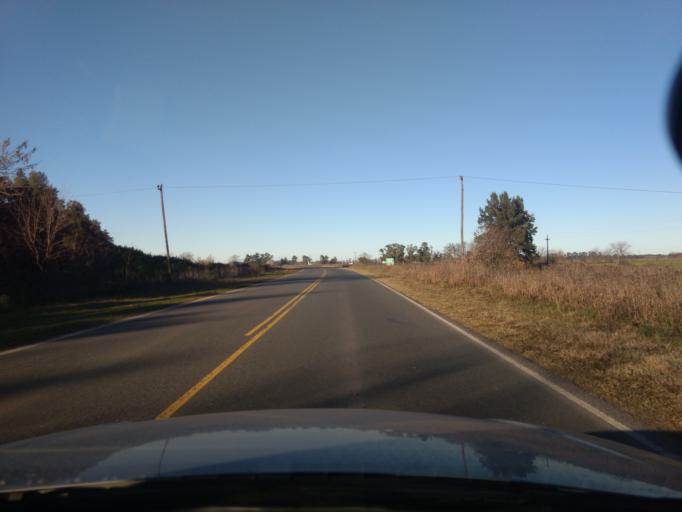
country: AR
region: Buenos Aires
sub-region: Partido de Lujan
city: Lujan
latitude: -34.6275
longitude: -59.1088
